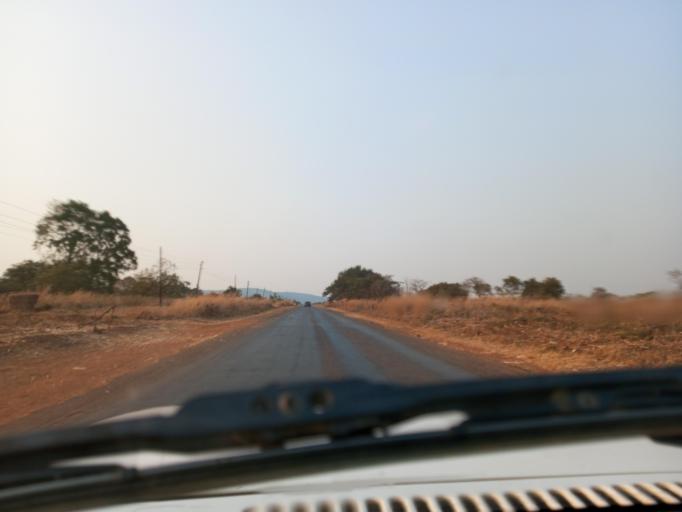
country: ZM
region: Northern
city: Mpika
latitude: -11.9083
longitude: 31.4146
